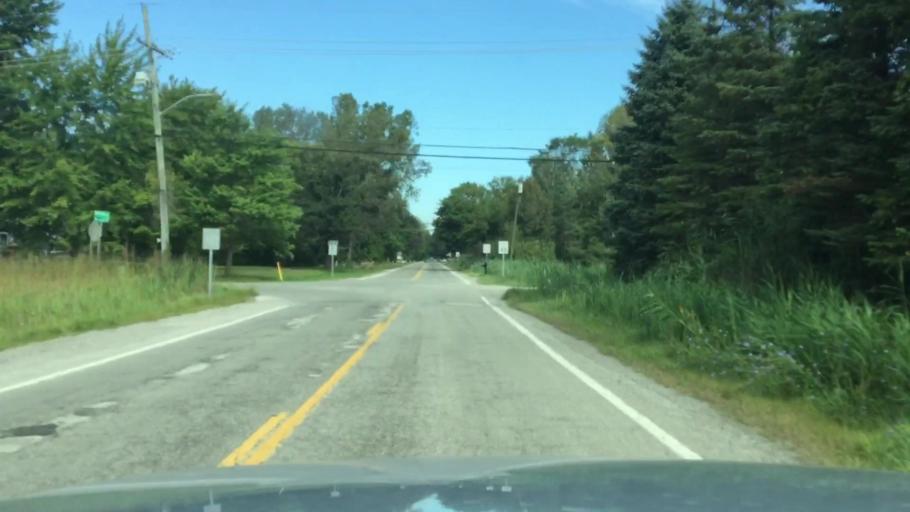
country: US
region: Michigan
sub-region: Wayne County
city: Belleville
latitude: 42.1598
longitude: -83.4614
